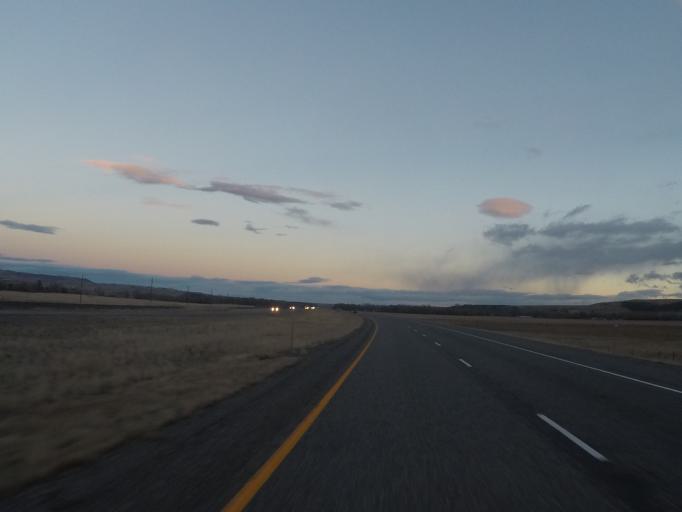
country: US
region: Montana
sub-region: Sweet Grass County
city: Big Timber
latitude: 45.8010
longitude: -109.8494
